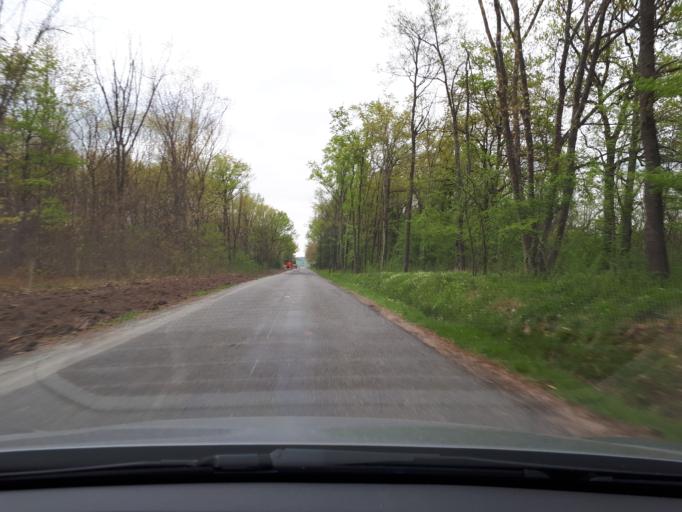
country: FR
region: Rhone-Alpes
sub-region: Departement de la Loire
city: Feurs
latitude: 45.7254
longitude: 4.2917
